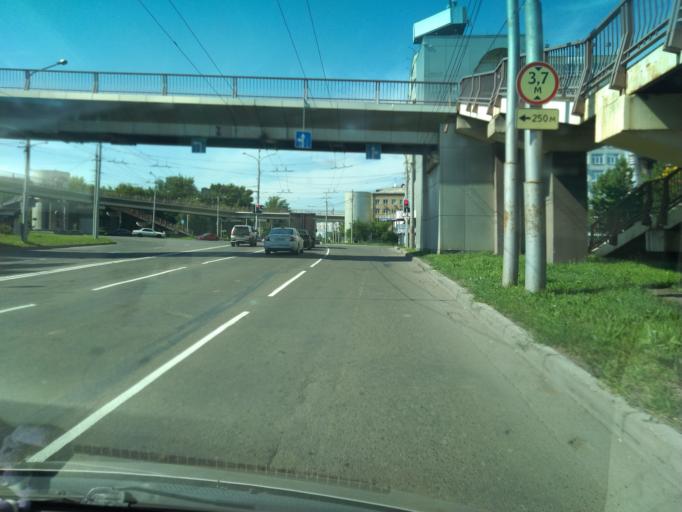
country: RU
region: Krasnoyarskiy
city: Krasnoyarsk
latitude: 56.0241
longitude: 92.8341
